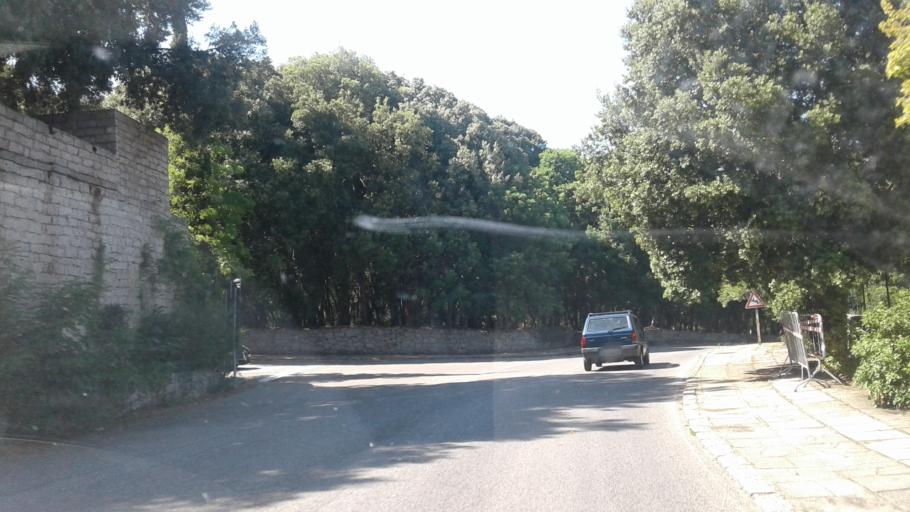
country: IT
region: Sardinia
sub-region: Provincia di Olbia-Tempio
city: Aggius
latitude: 40.9336
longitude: 9.0668
